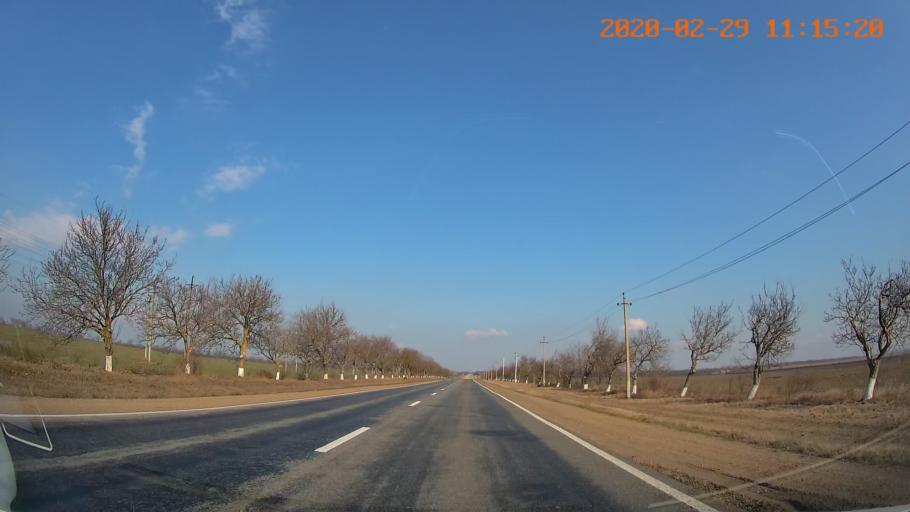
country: MD
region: Telenesti
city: Dubasari
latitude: 47.2931
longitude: 29.1648
